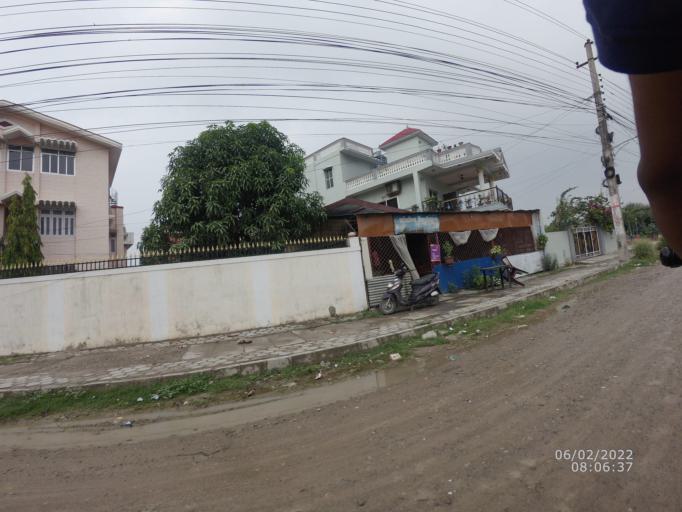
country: NP
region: Western Region
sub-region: Lumbini Zone
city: Bhairahawa
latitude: 27.4806
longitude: 83.4659
